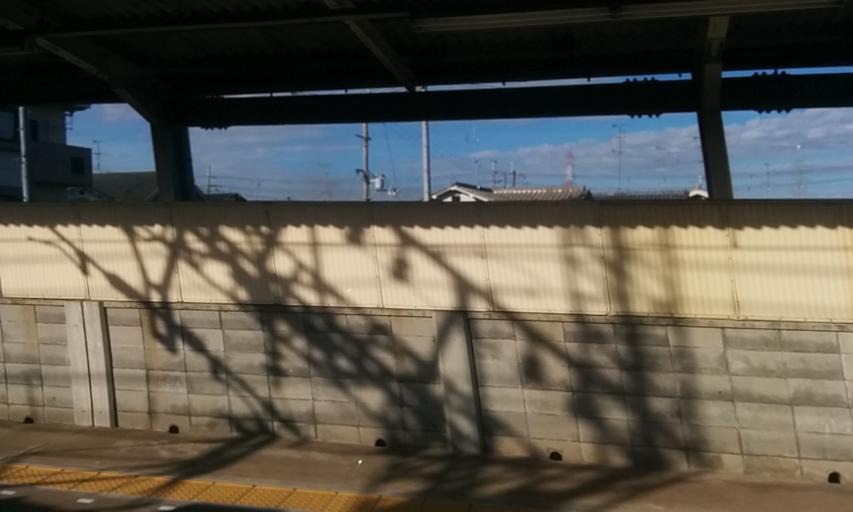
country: JP
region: Kyoto
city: Tanabe
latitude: 34.8410
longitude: 135.7729
